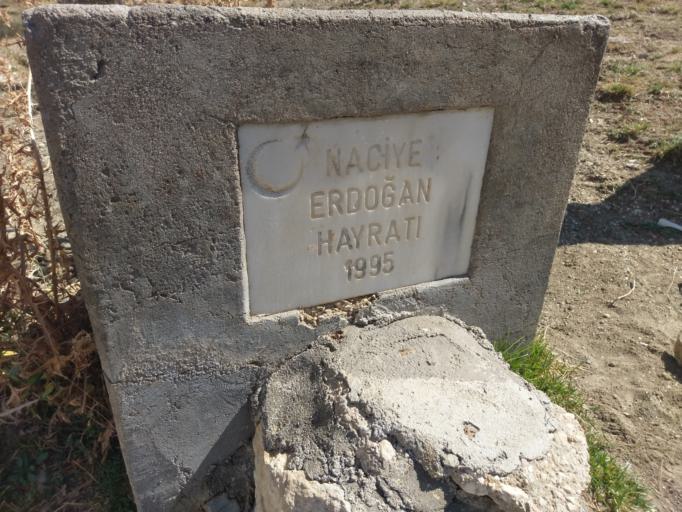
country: TR
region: Kayseri
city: Toklar
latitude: 38.3921
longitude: 36.0949
